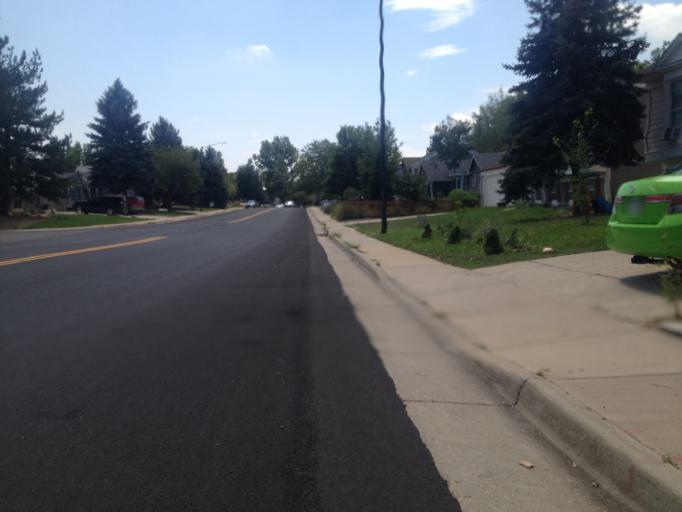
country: US
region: Colorado
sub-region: Boulder County
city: Louisville
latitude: 39.9716
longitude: -105.1511
